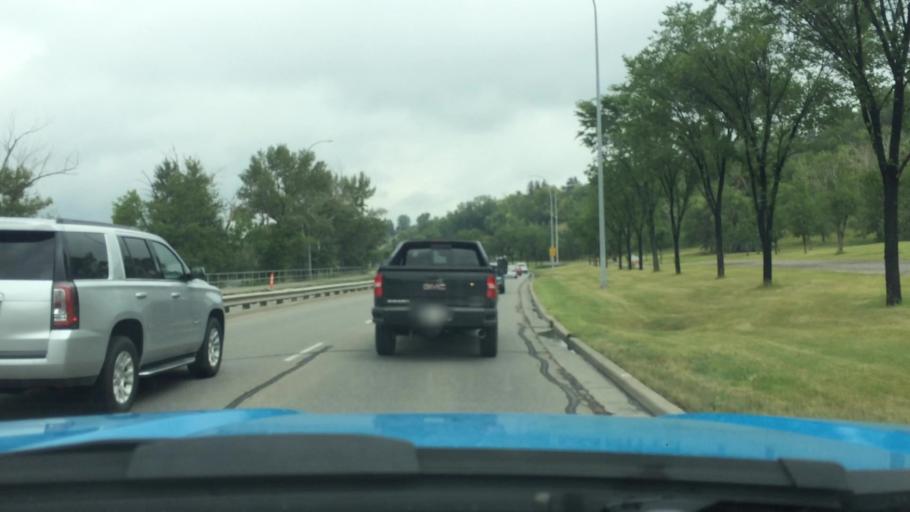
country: CA
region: Alberta
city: Calgary
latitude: 51.0552
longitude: -114.0639
